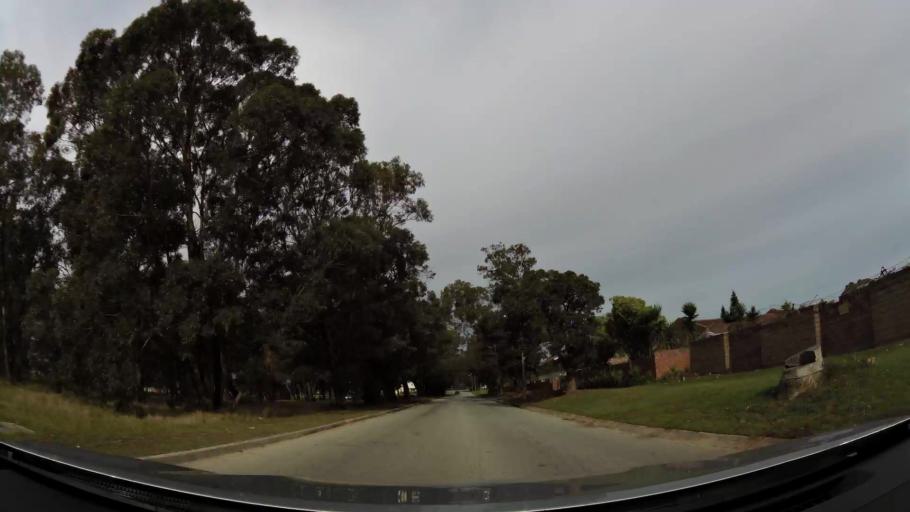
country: ZA
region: Eastern Cape
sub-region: Nelson Mandela Bay Metropolitan Municipality
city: Port Elizabeth
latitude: -33.9376
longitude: 25.4942
